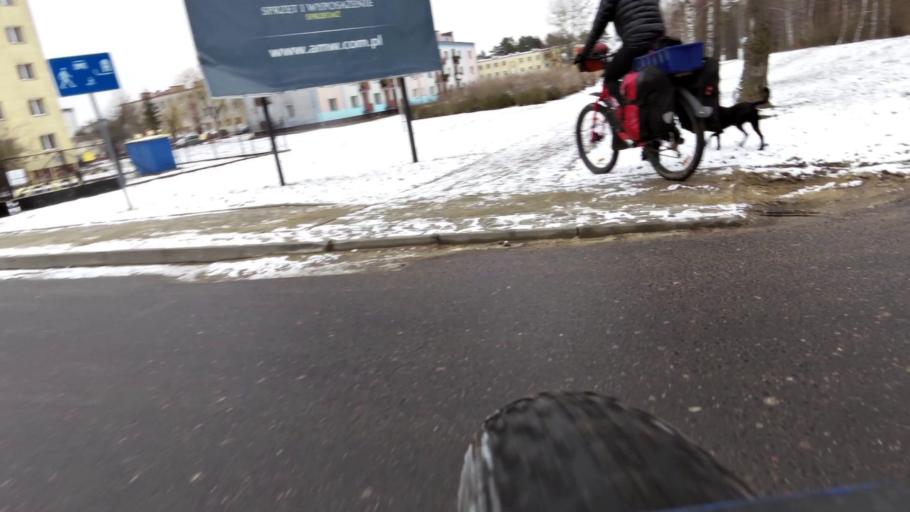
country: PL
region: West Pomeranian Voivodeship
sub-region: Powiat walecki
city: Miroslawiec
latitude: 53.3704
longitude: 16.0852
